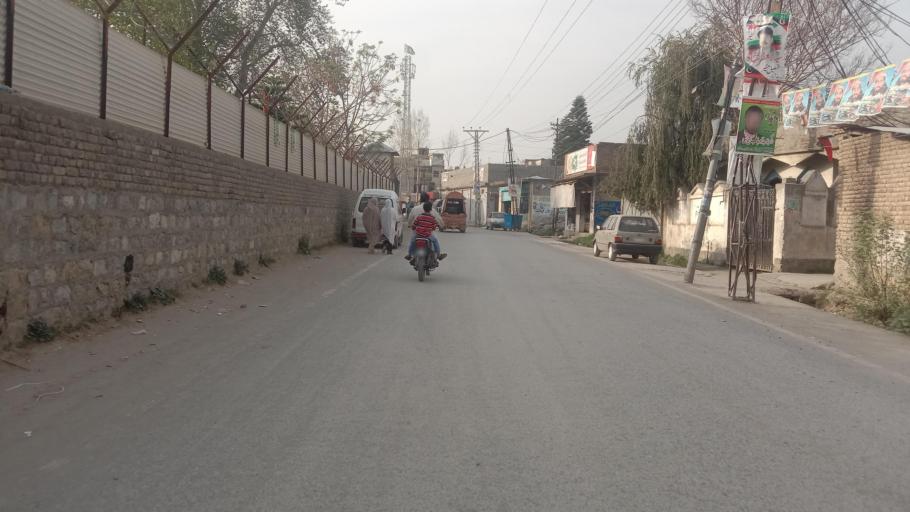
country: PK
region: Khyber Pakhtunkhwa
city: Abbottabad
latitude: 34.1609
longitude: 73.2631
